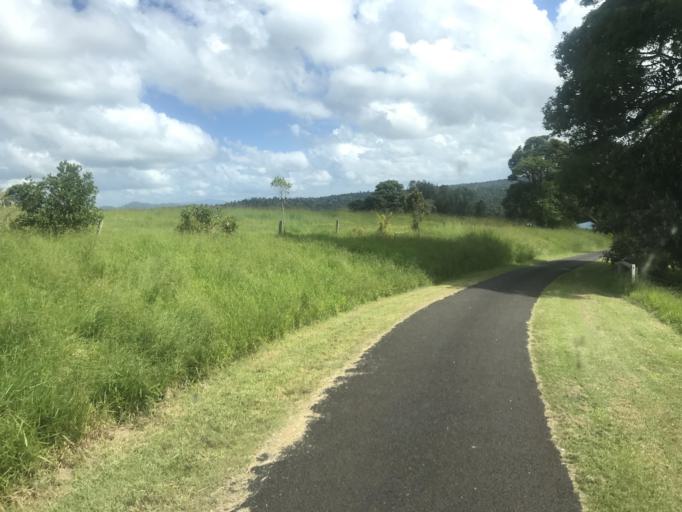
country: AU
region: Queensland
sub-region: Tablelands
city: Ravenshoe
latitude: -17.5473
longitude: 145.6981
